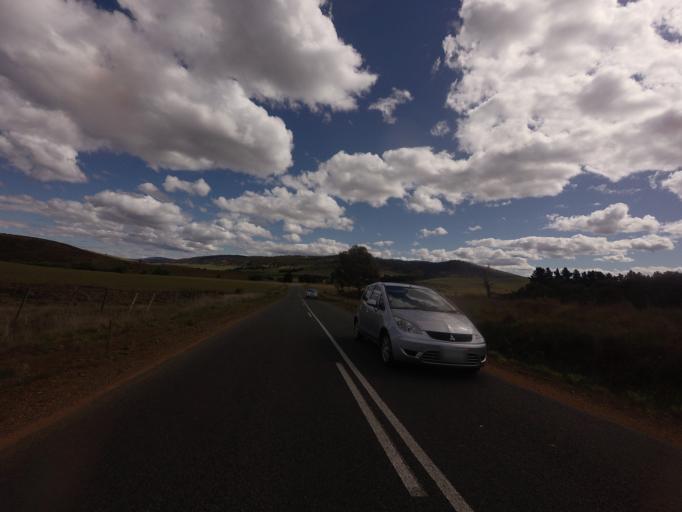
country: AU
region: Tasmania
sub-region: Brighton
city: Bridgewater
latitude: -42.3978
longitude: 147.3138
